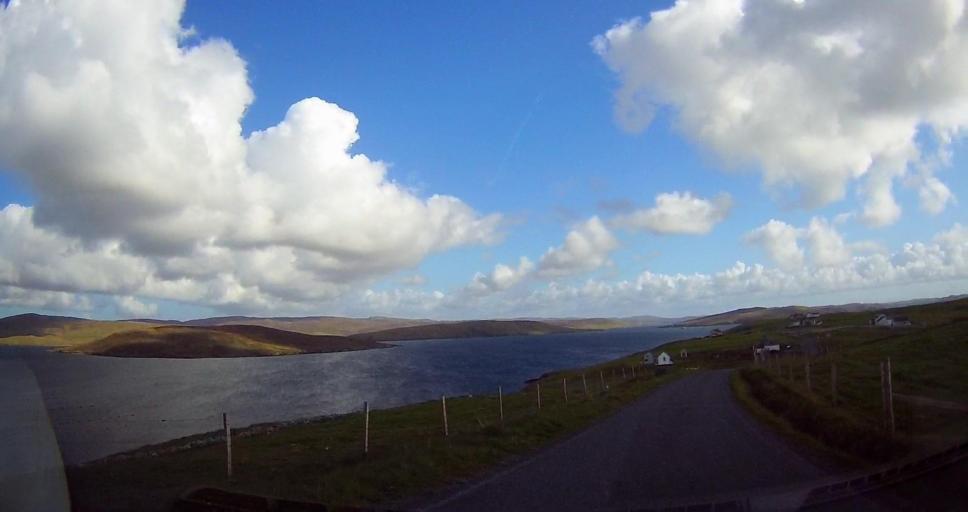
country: GB
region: Scotland
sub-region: Shetland Islands
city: Lerwick
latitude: 60.3677
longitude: -1.3817
